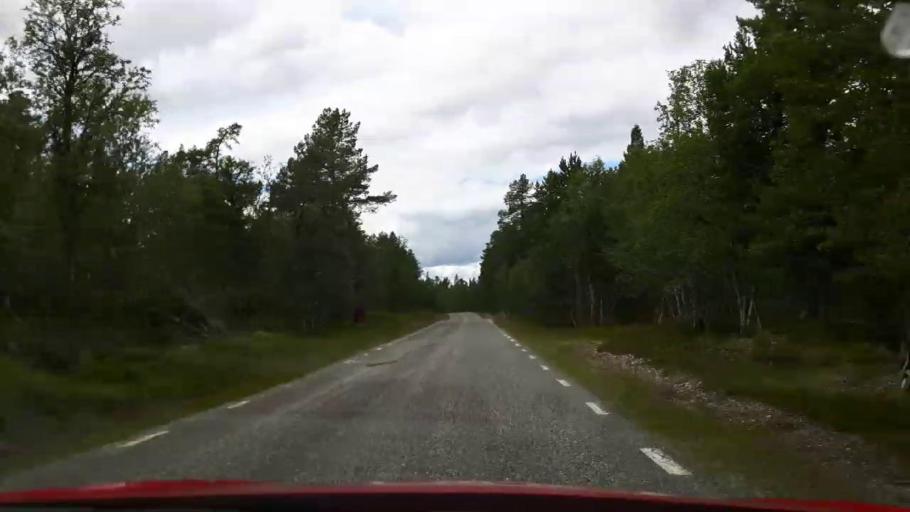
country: NO
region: Hedmark
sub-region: Engerdal
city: Engerdal
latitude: 62.2827
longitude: 12.8493
